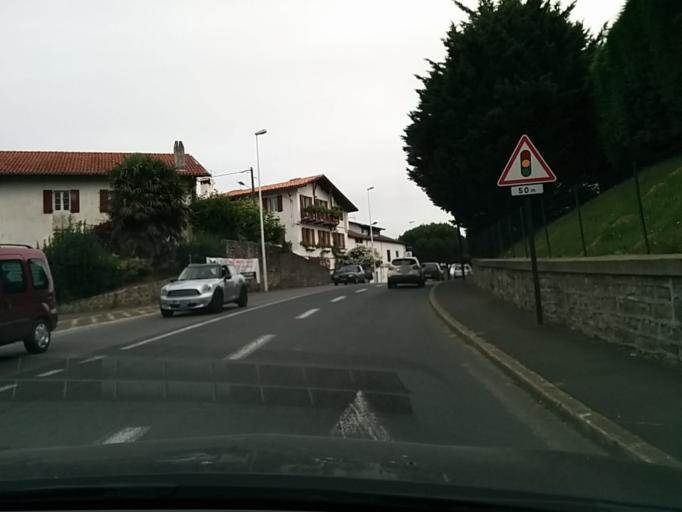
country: FR
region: Aquitaine
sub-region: Departement des Pyrenees-Atlantiques
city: Guethary
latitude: 43.4201
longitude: -1.6074
